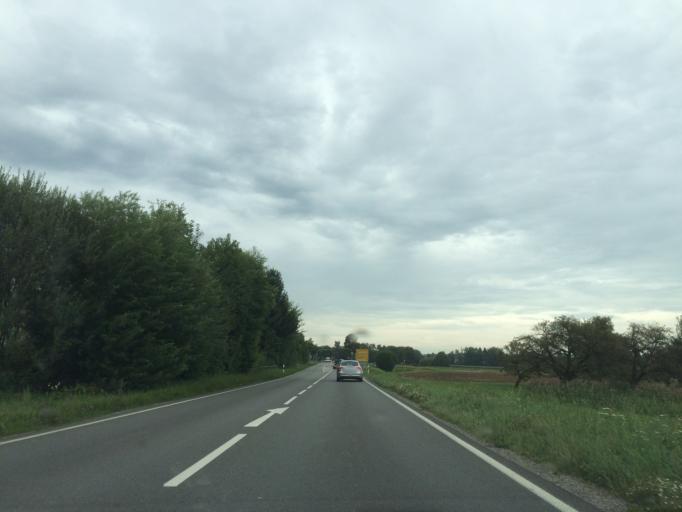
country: DE
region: Baden-Wuerttemberg
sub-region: Tuebingen Region
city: Oberteuringen
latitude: 47.7323
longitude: 9.4623
